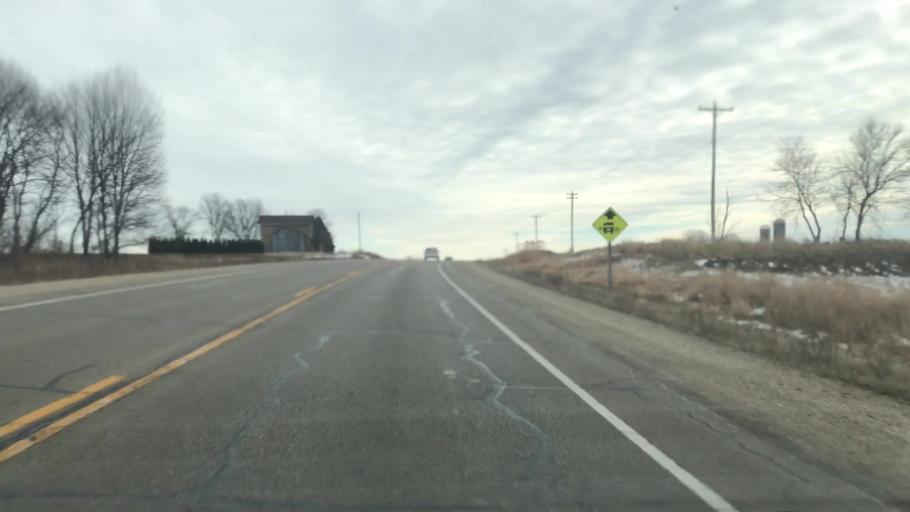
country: US
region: Wisconsin
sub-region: Dodge County
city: Theresa
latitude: 43.4304
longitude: -88.4455
